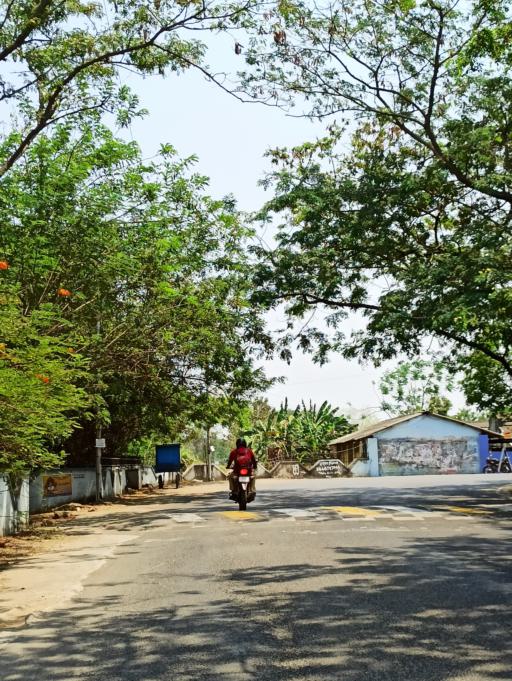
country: IN
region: Tamil Nadu
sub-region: Thiruvallur
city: Chinnasekkadu
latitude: 13.1620
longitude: 80.2450
